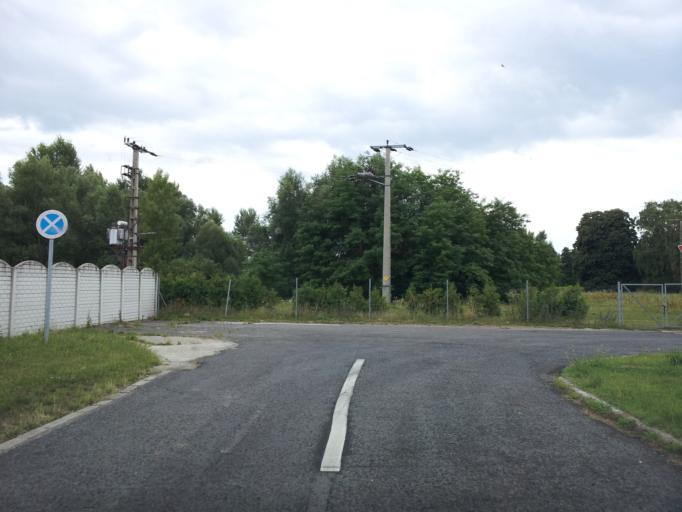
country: HU
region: Vas
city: Janoshaza
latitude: 47.0944
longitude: 17.0515
